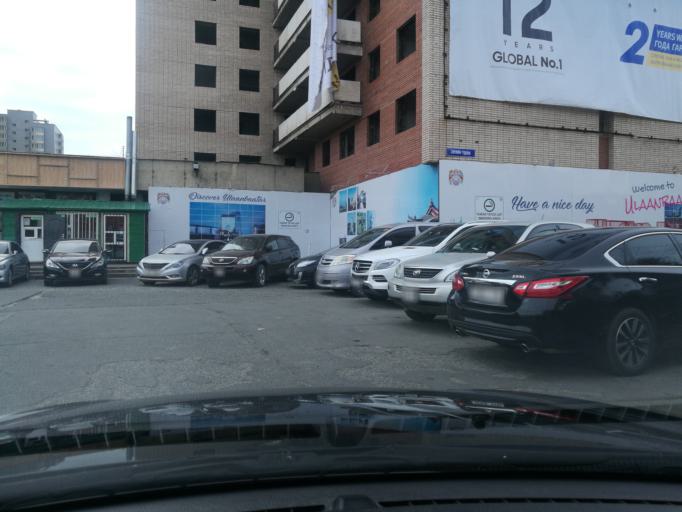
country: MN
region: Ulaanbaatar
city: Ulaanbaatar
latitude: 47.9134
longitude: 106.9055
